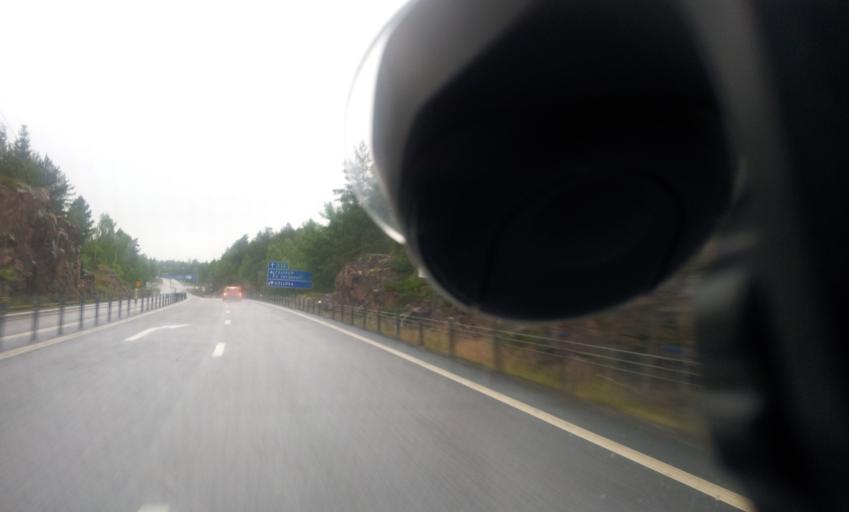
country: SE
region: OEstergoetland
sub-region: Valdemarsviks Kommun
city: Valdemarsvik
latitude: 58.1547
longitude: 16.5439
